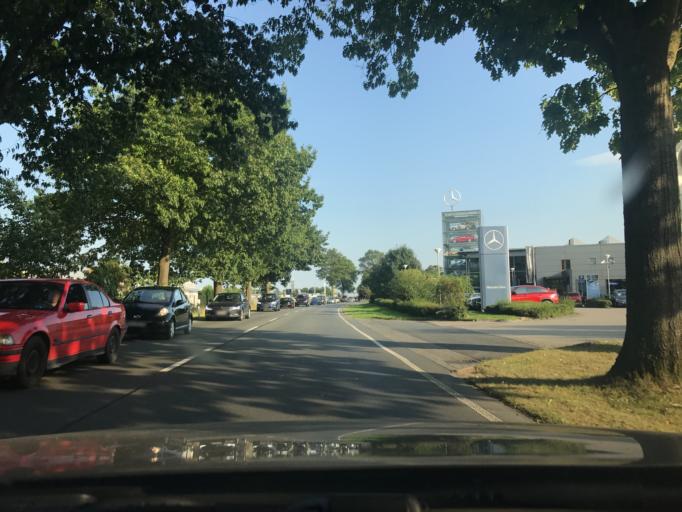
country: DE
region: North Rhine-Westphalia
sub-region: Regierungsbezirk Dusseldorf
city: Kevelaer
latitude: 51.5841
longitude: 6.2542
